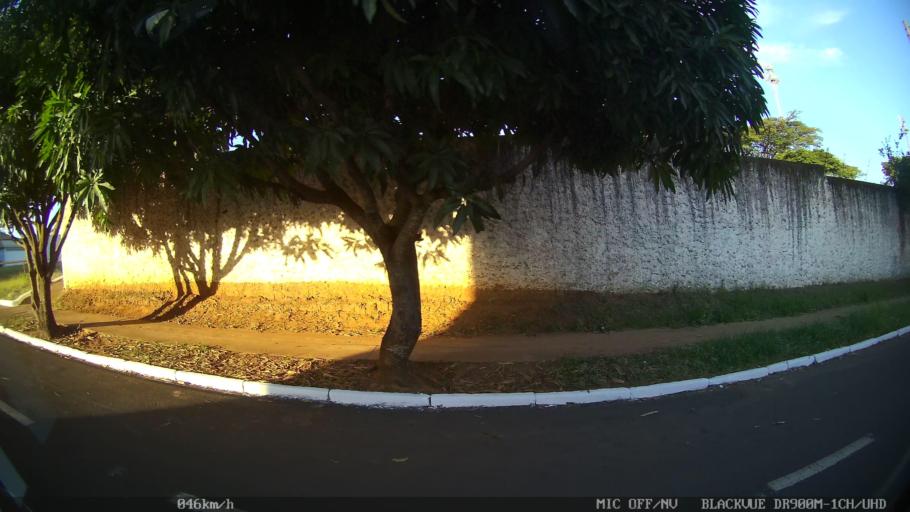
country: BR
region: Sao Paulo
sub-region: Franca
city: Franca
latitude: -20.5349
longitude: -47.3863
